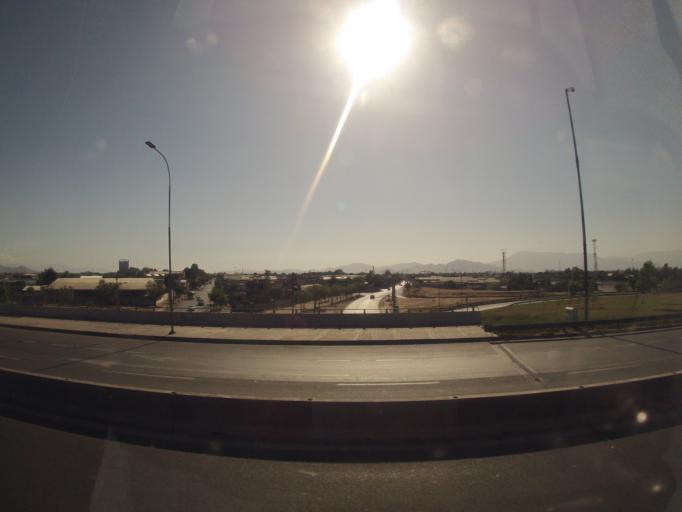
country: CL
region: Santiago Metropolitan
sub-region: Provincia de Santiago
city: Santiago
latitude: -33.4779
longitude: -70.6857
